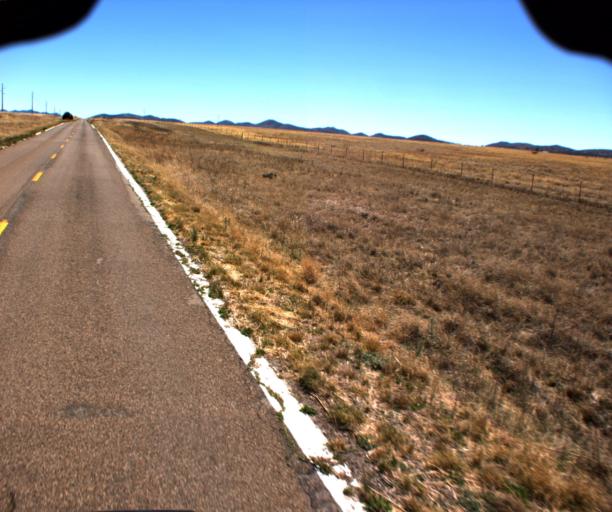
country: US
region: Arizona
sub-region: Cochise County
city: Huachuca City
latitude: 31.6351
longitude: -110.5973
